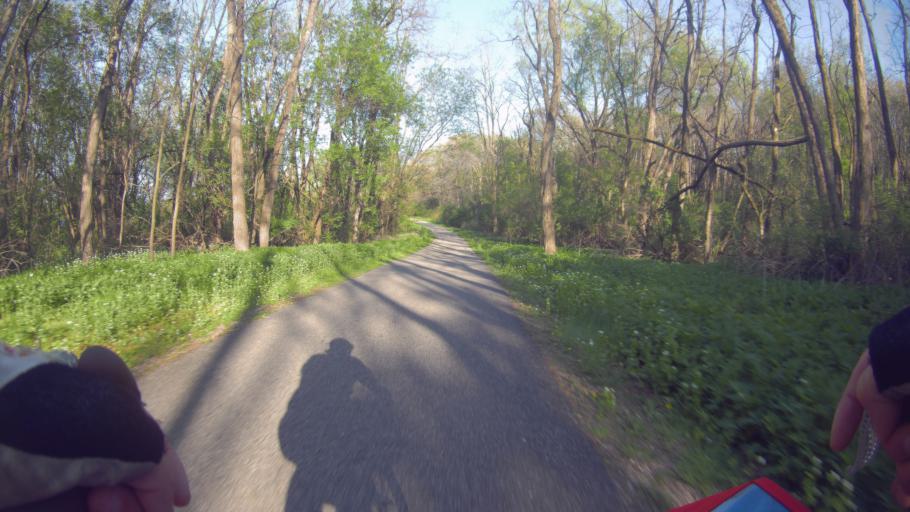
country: US
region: Wisconsin
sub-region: Dane County
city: Shorewood Hills
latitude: 43.0214
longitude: -89.4570
